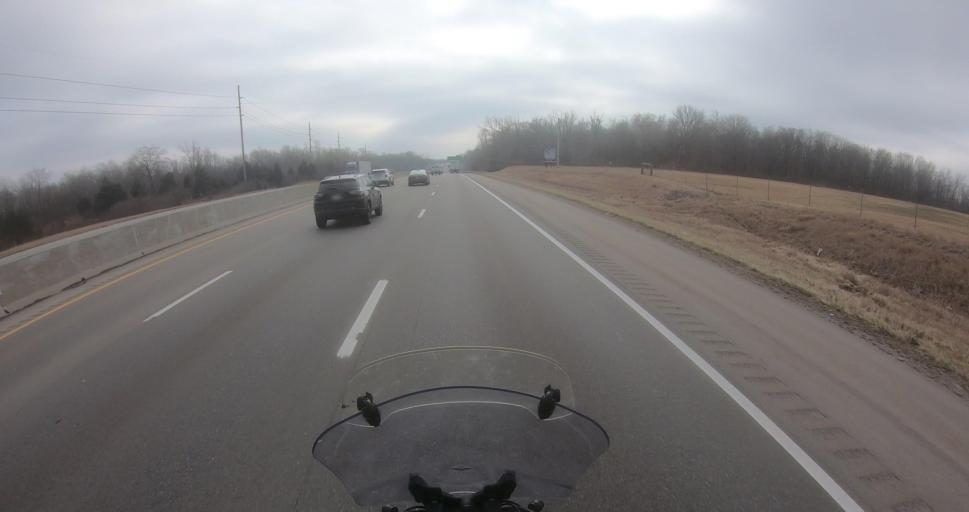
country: US
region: Ohio
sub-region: Montgomery County
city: Vandalia
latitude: 39.9205
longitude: -84.1883
